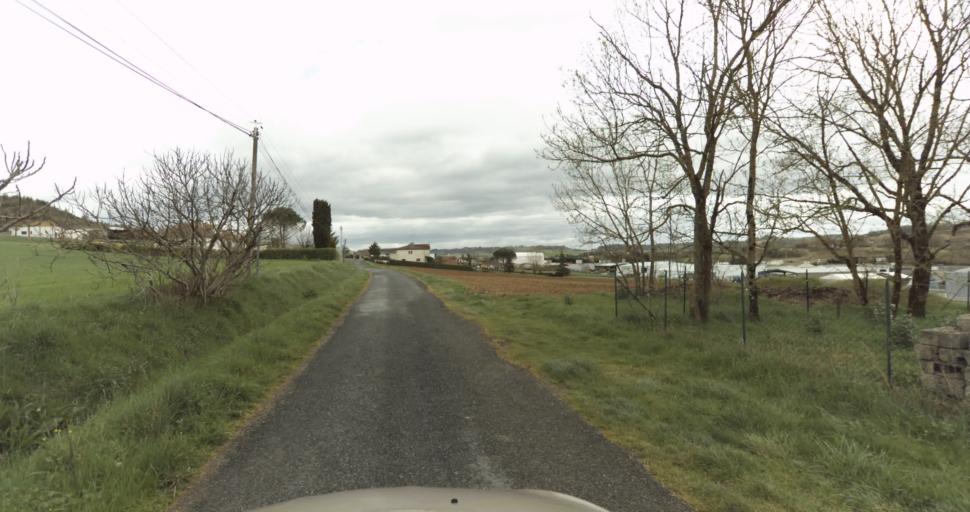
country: FR
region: Midi-Pyrenees
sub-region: Departement du Tarn
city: Puygouzon
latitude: 43.8948
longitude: 2.1615
